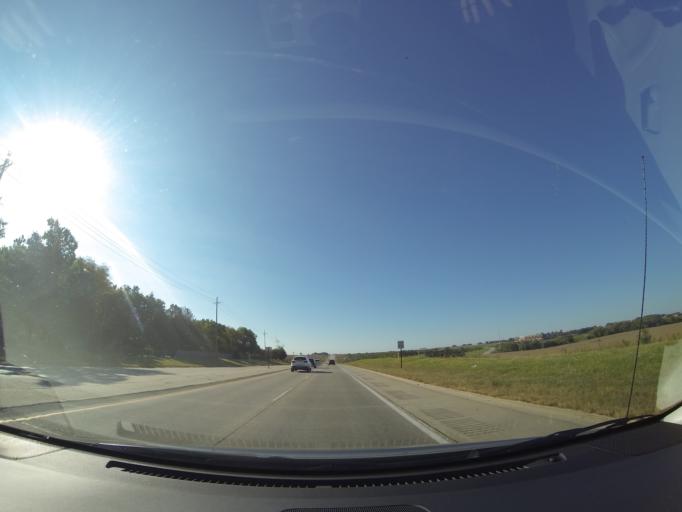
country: US
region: Nebraska
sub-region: Sarpy County
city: Gretna
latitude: 41.2039
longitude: -96.2344
